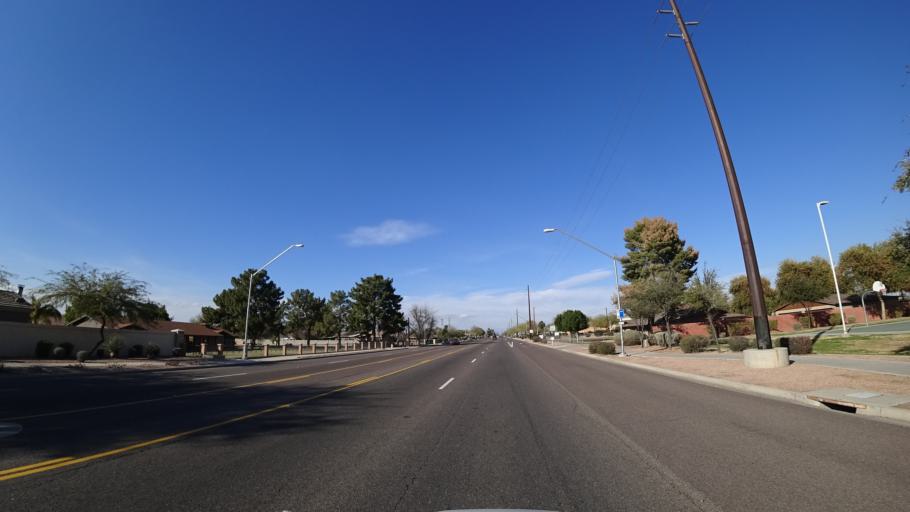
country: US
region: Arizona
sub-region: Maricopa County
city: Glendale
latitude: 33.5259
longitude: -112.2376
